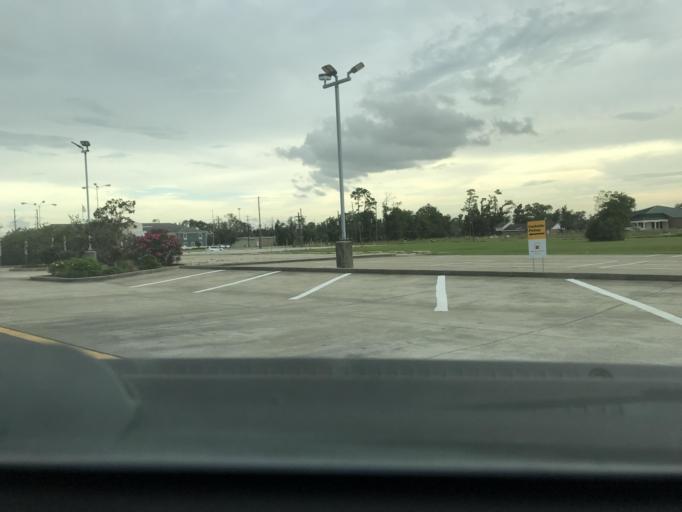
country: US
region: Louisiana
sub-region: Calcasieu Parish
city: Westlake
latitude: 30.2546
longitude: -93.2588
